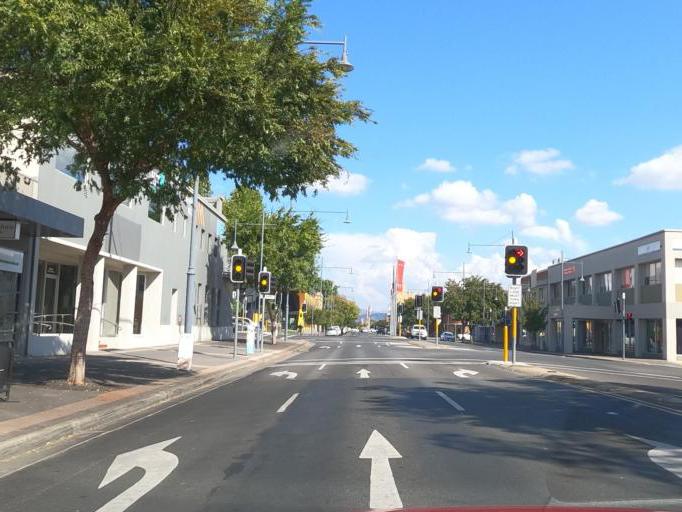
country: AU
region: New South Wales
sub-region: Albury Municipality
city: Albury
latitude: -36.0780
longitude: 146.9162
